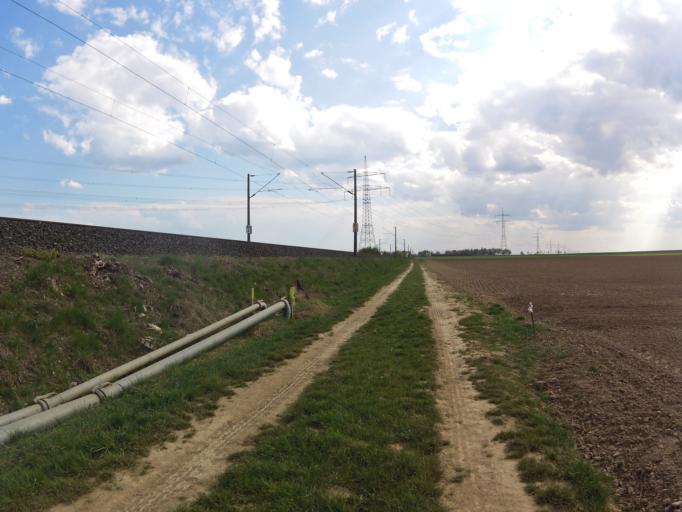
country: DE
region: Bavaria
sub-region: Regierungsbezirk Unterfranken
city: Oberpleichfeld
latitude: 49.8671
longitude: 10.0999
